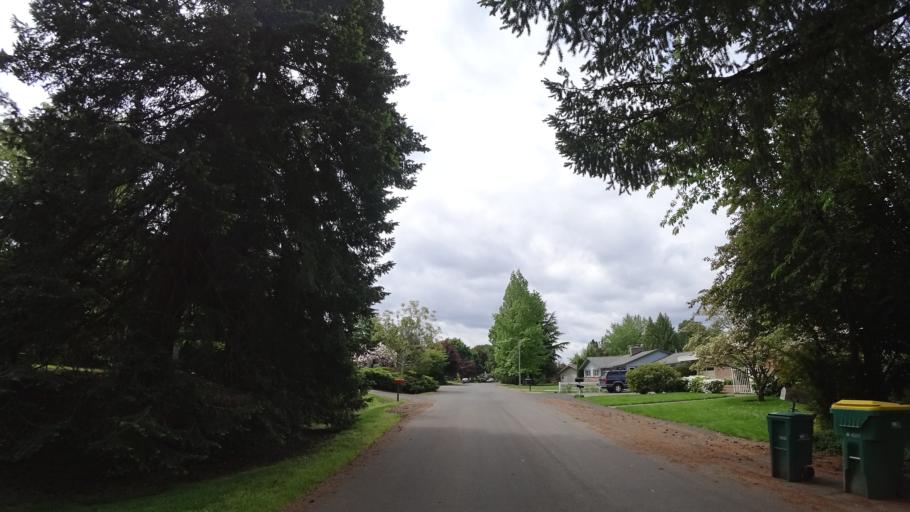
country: US
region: Oregon
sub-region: Washington County
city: Garden Home-Whitford
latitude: 45.4633
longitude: -122.7758
